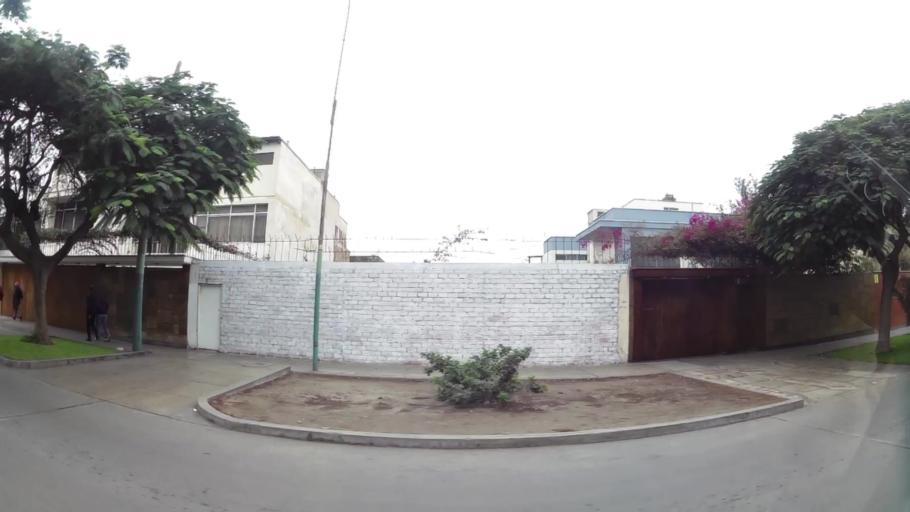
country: PE
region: Lima
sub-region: Lima
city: San Luis
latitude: -12.0906
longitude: -77.0015
